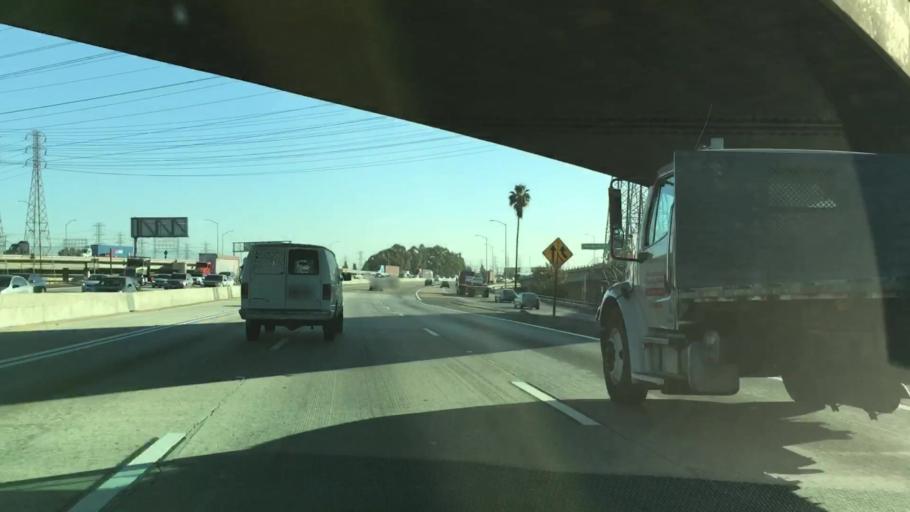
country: US
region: California
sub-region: Los Angeles County
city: East Rancho Dominguez
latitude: 33.8731
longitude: -118.1985
